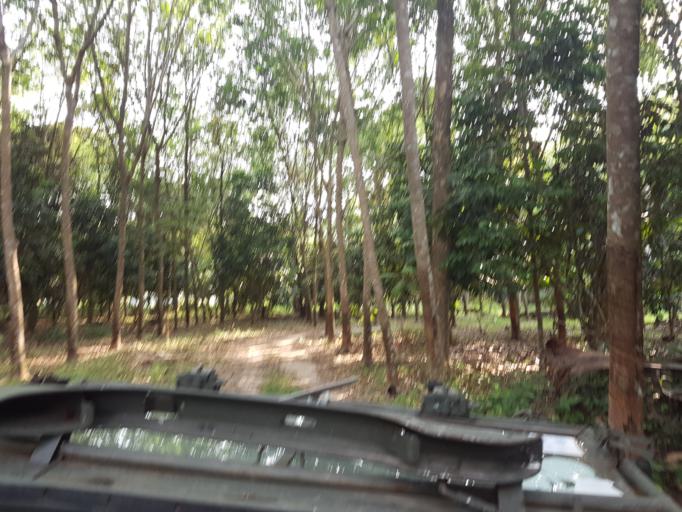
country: TH
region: Pattani
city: Khok Pho
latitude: 6.6657
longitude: 101.0922
